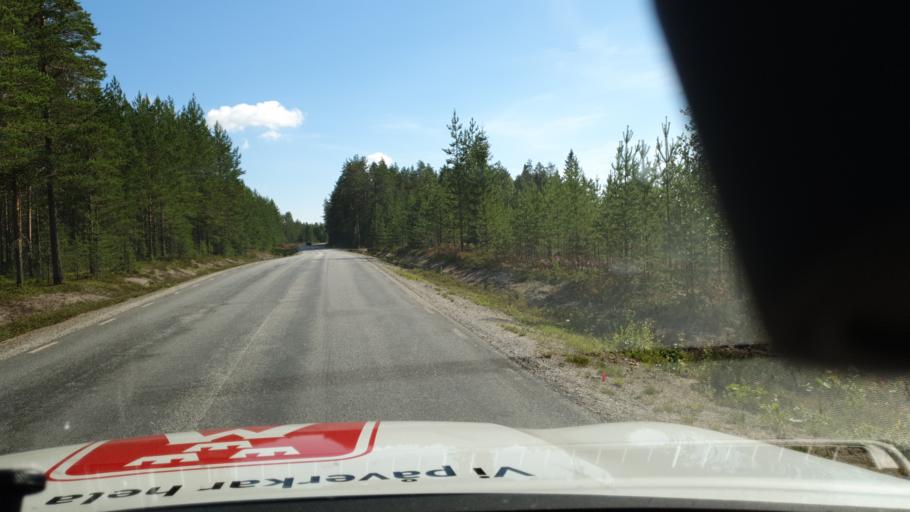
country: SE
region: Vaesterbotten
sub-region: Umea Kommun
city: Roback
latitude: 63.9774
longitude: 20.1173
